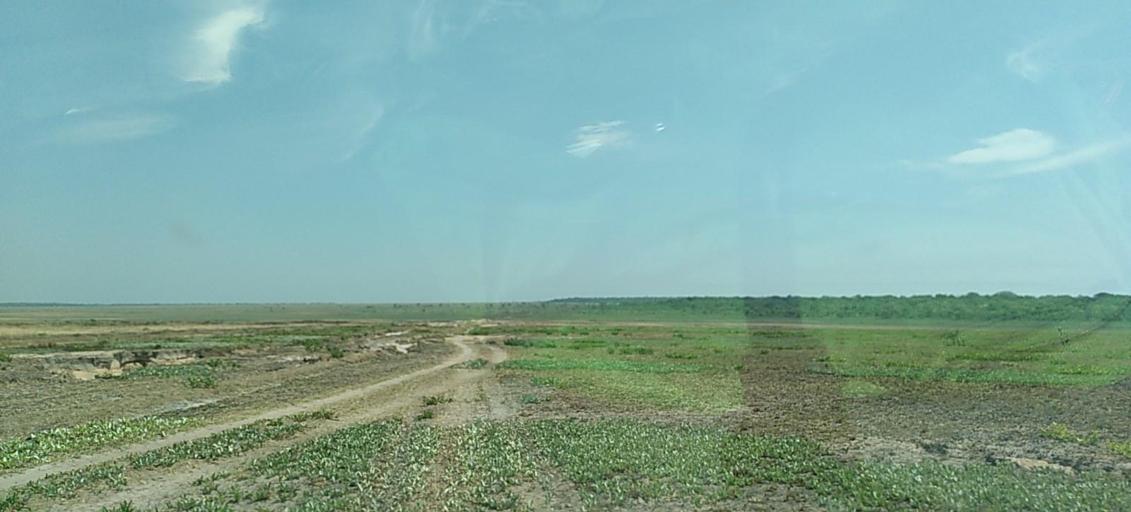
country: ZM
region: North-Western
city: Mwinilunga
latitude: -11.6723
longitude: 25.2069
